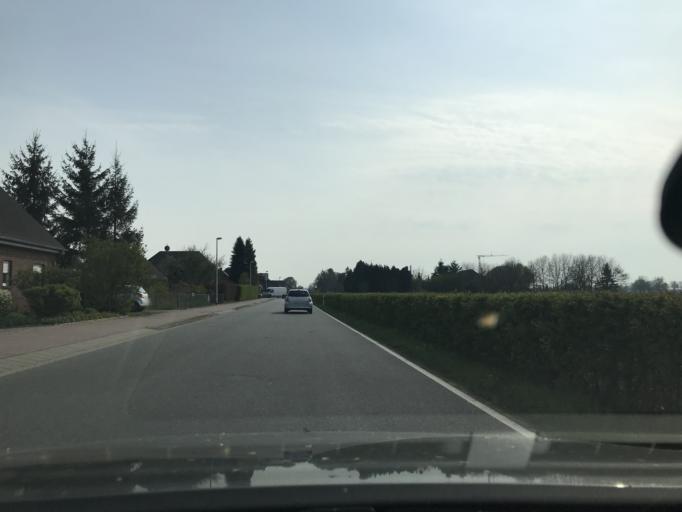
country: DE
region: North Rhine-Westphalia
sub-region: Regierungsbezirk Dusseldorf
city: Goch
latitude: 51.7217
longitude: 6.1660
